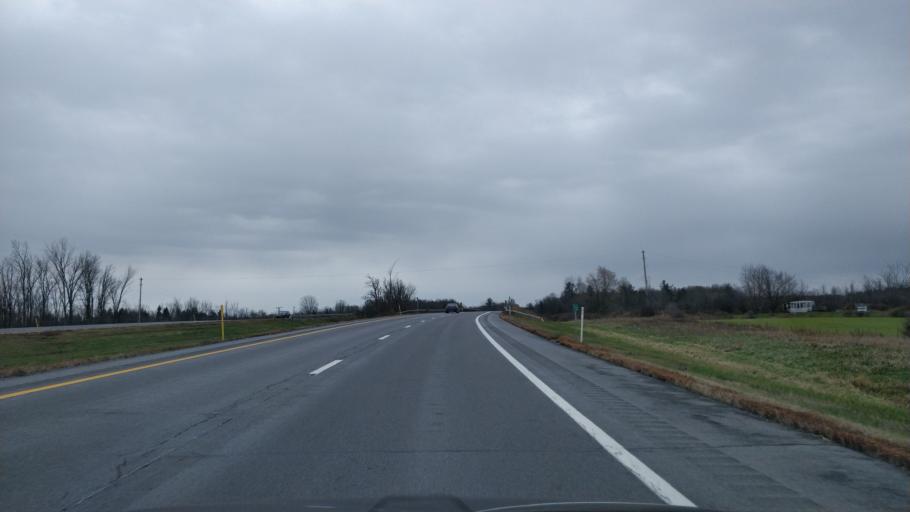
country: US
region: New York
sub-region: Jefferson County
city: Calcium
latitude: 44.1393
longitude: -75.8824
